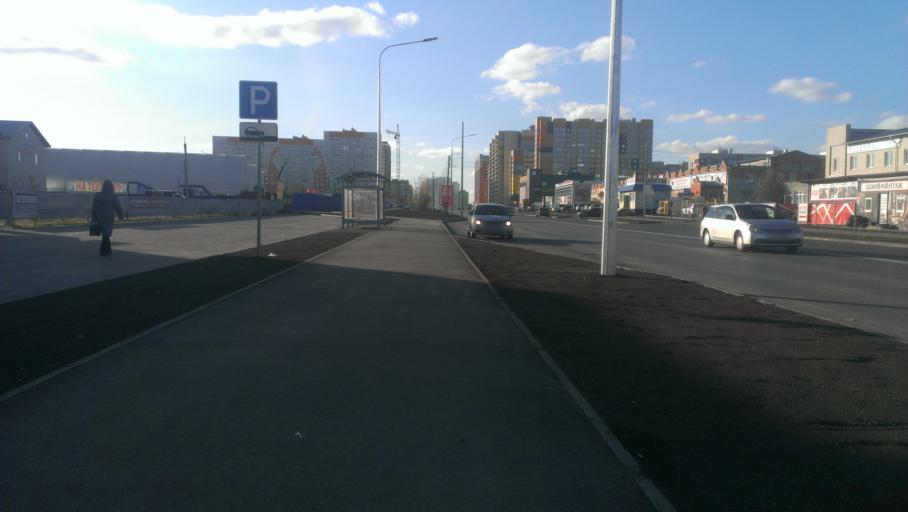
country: RU
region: Altai Krai
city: Novosilikatnyy
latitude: 53.3363
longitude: 83.6660
